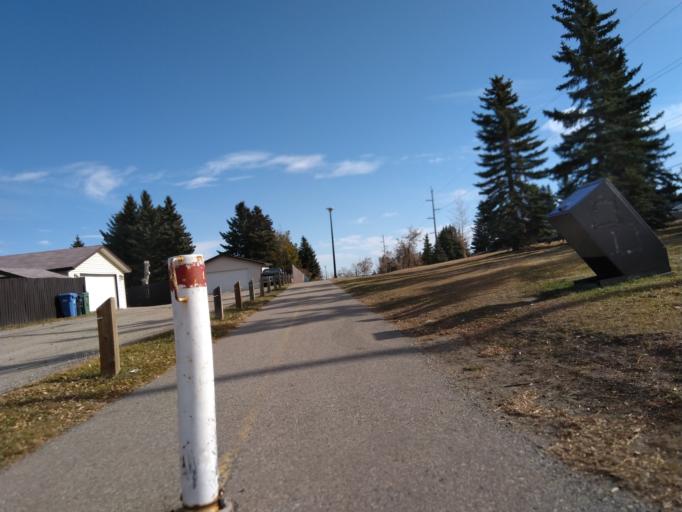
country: CA
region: Alberta
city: Calgary
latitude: 51.1252
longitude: -114.0853
